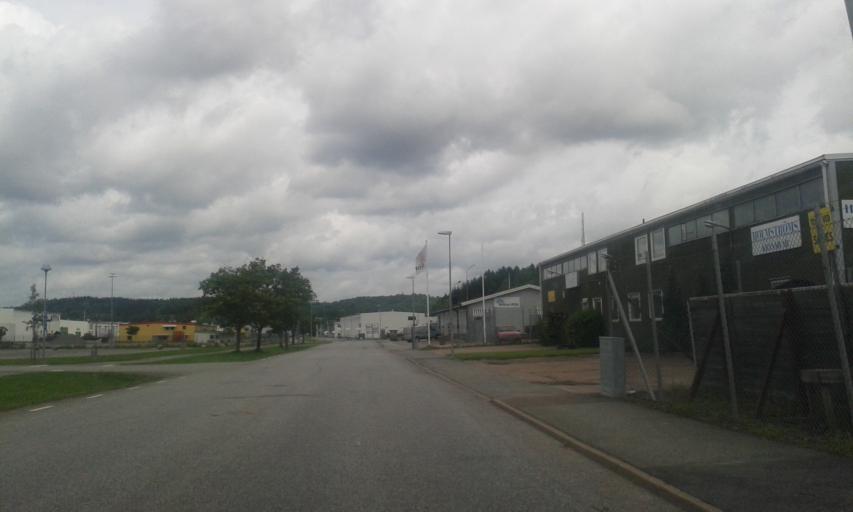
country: SE
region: Vaestra Goetaland
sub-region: Kungalvs Kommun
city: Kungalv
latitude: 57.8728
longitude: 11.9432
